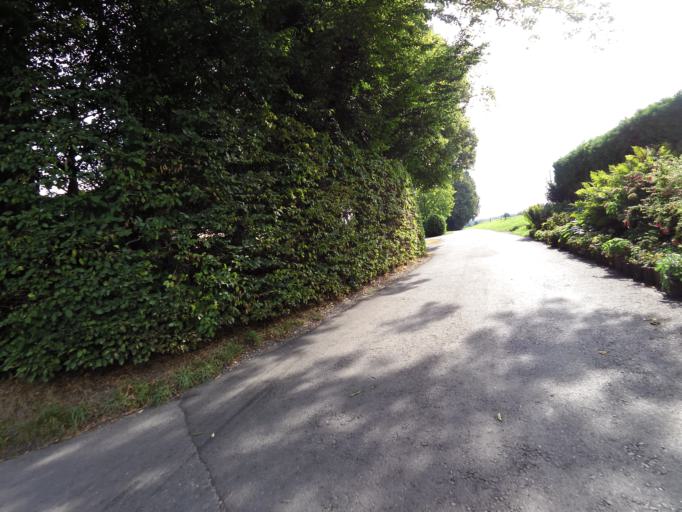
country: CH
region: Thurgau
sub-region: Kreuzlingen District
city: Tagerwilen
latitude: 47.6433
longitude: 9.1433
